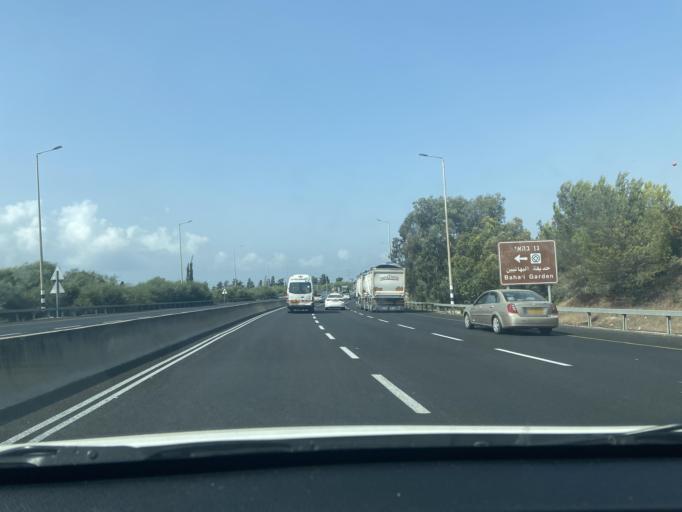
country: IL
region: Northern District
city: `Akko
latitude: 32.9496
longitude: 35.0919
